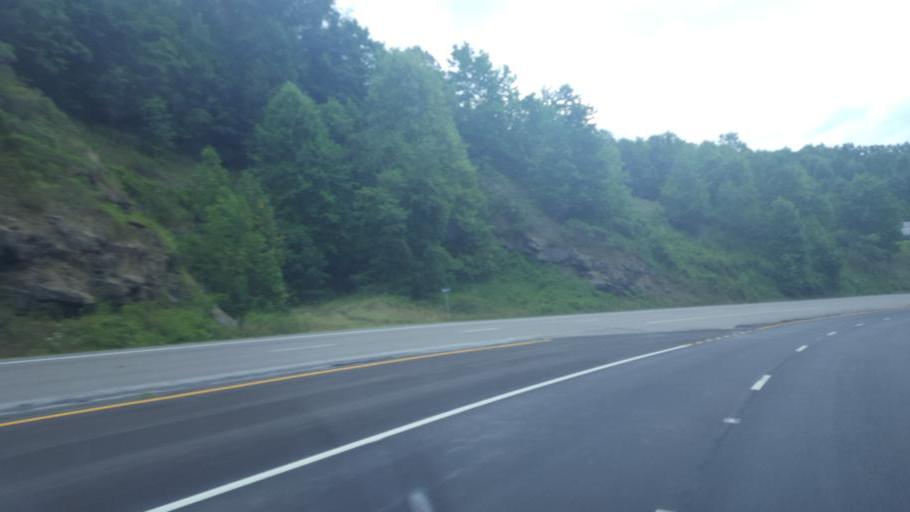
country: US
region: Kentucky
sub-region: Letcher County
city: Jenkins
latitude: 37.1572
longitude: -82.6191
